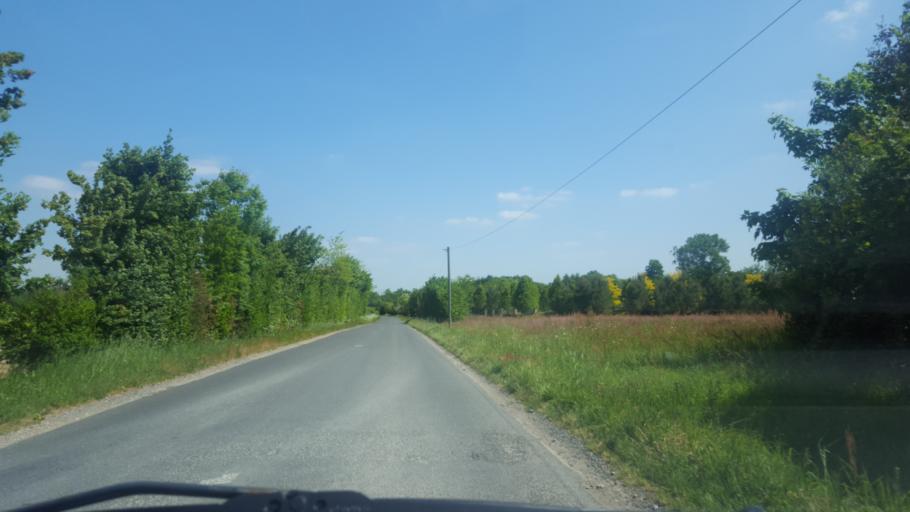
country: FR
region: Pays de la Loire
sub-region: Departement de la Loire-Atlantique
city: La Limouziniere
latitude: 47.0378
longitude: -1.5955
